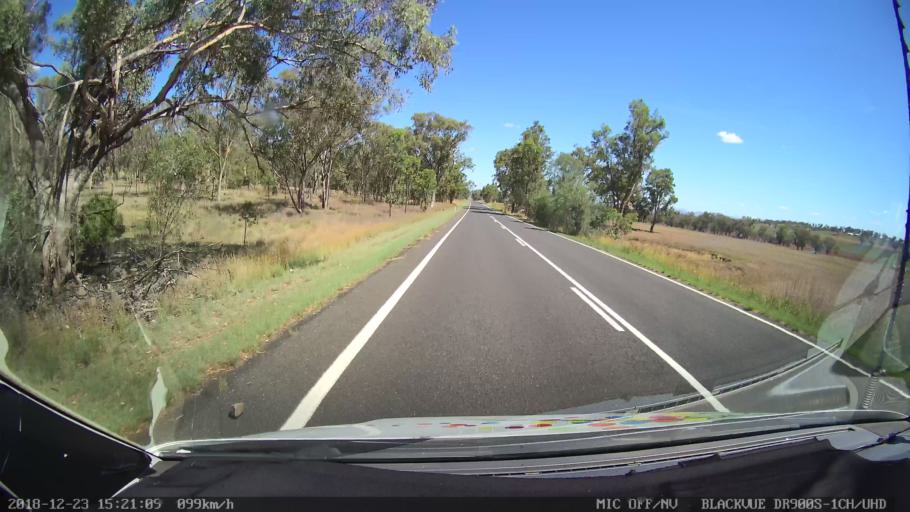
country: AU
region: New South Wales
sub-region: Tamworth Municipality
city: Manilla
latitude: -30.8525
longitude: 150.7946
